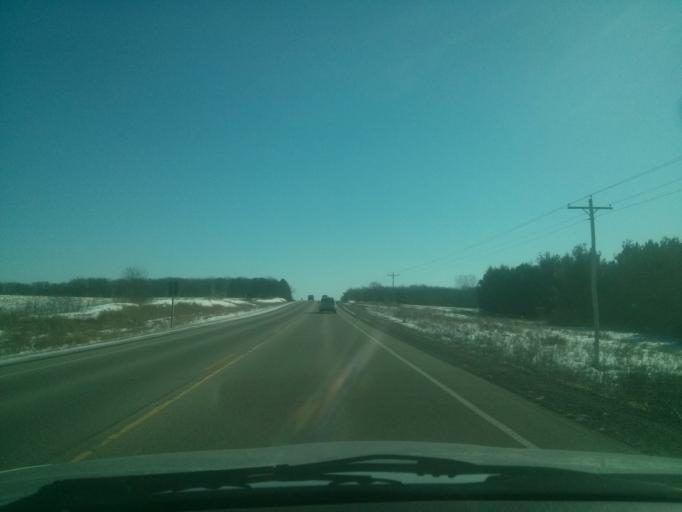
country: US
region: Wisconsin
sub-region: Saint Croix County
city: New Richmond
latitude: 45.1369
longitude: -92.4309
